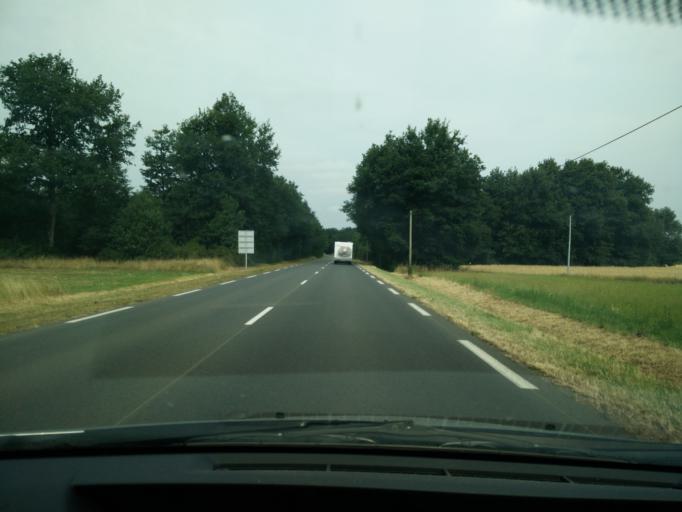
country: FR
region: Pays de la Loire
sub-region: Departement de Maine-et-Loire
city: Vaudelnay
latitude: 47.1567
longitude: -0.1873
